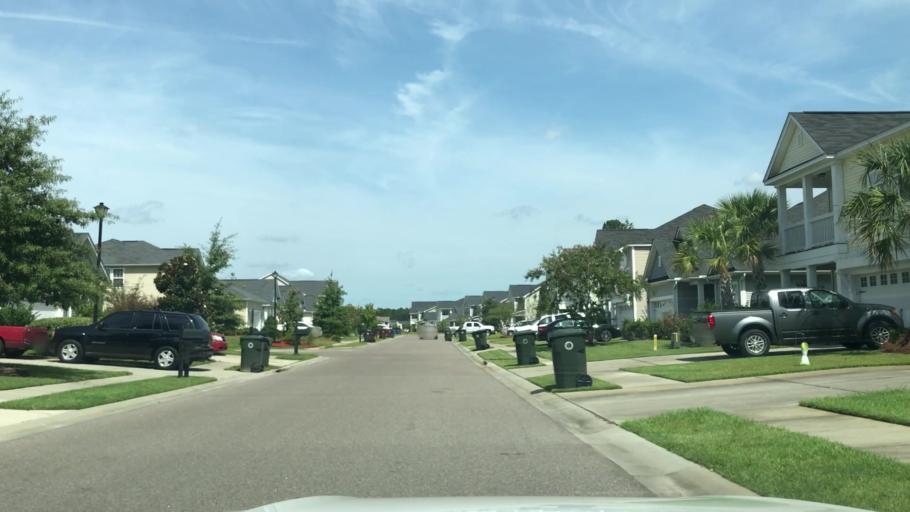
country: US
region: South Carolina
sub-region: Berkeley County
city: Moncks Corner
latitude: 33.1051
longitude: -80.0410
